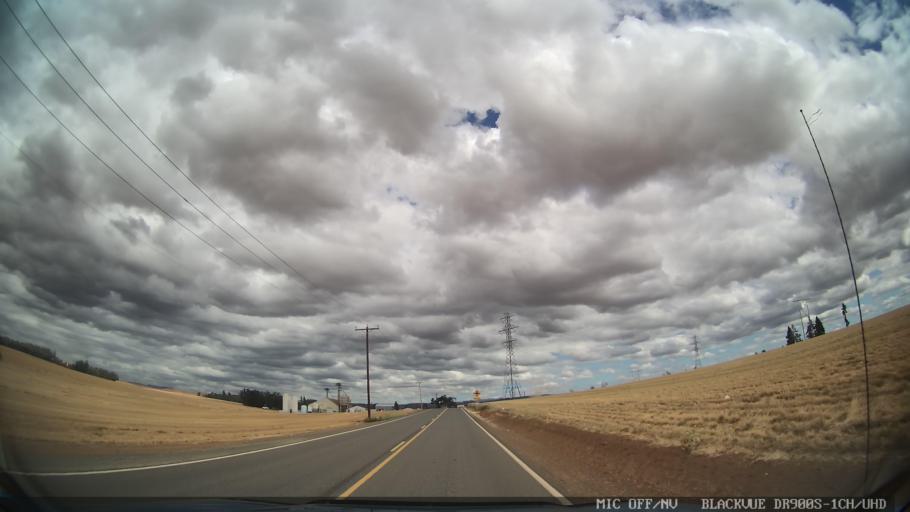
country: US
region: Oregon
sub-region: Marion County
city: Sublimity
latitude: 44.8663
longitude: -122.7952
